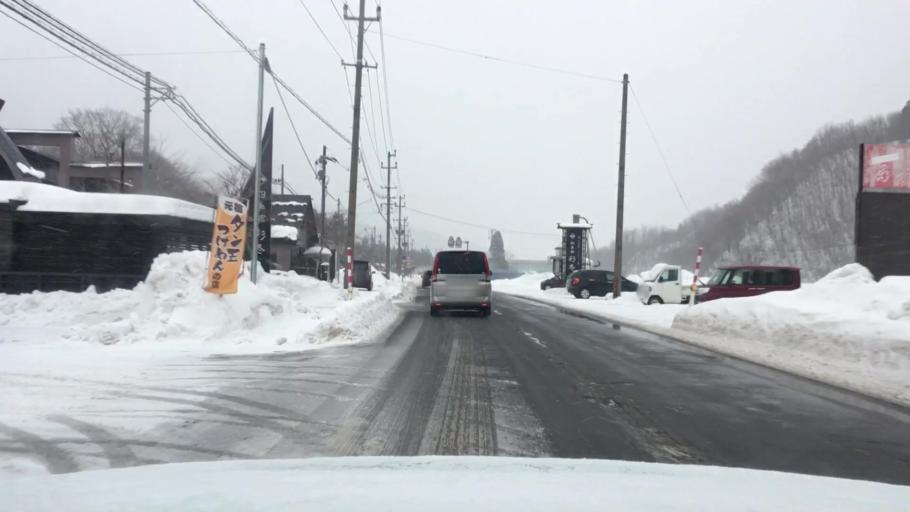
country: JP
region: Akita
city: Hanawa
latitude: 40.0430
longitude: 140.9984
